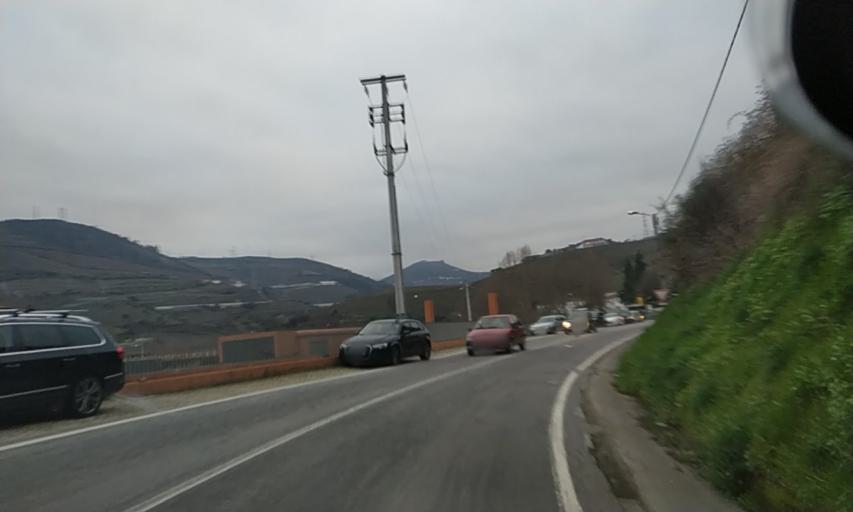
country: PT
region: Vila Real
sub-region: Peso da Regua
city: Peso da Regua
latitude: 41.1533
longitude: -7.7849
